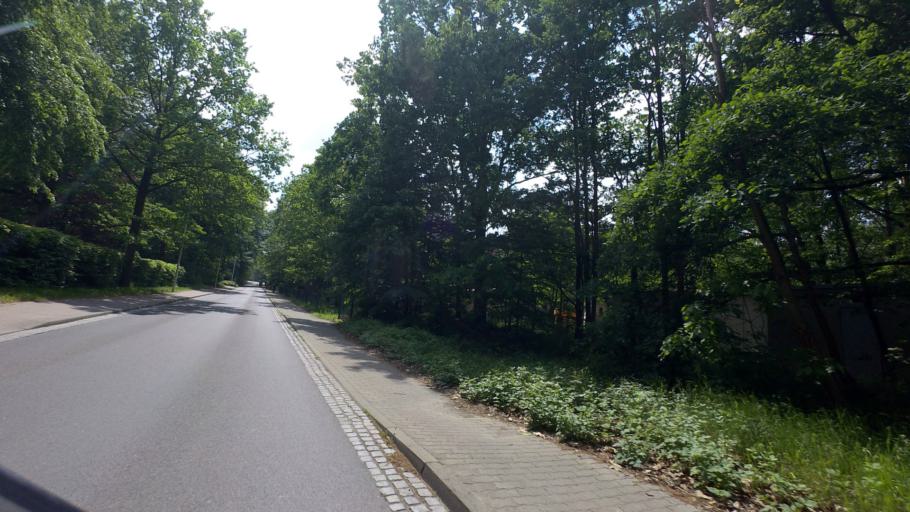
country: DE
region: Saxony
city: Weisswasser
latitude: 51.5019
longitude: 14.6153
